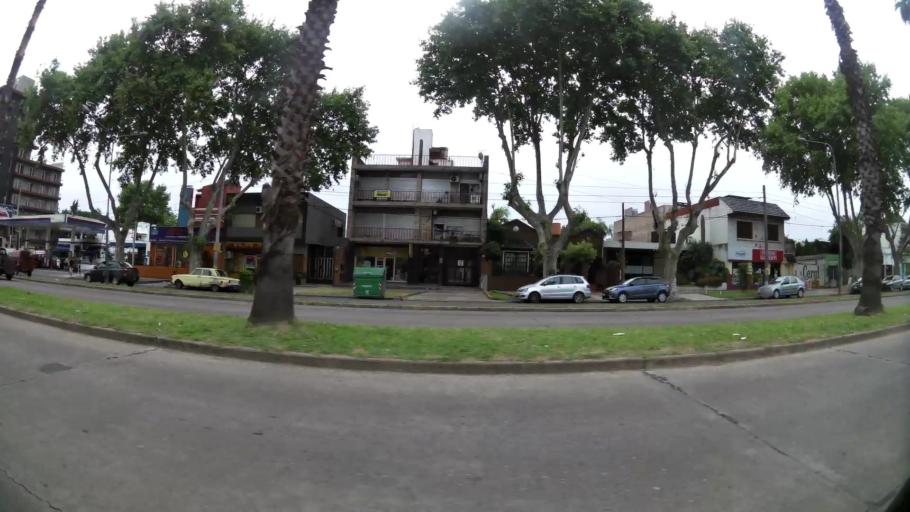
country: AR
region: Santa Fe
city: Granadero Baigorria
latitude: -32.9044
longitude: -60.6893
